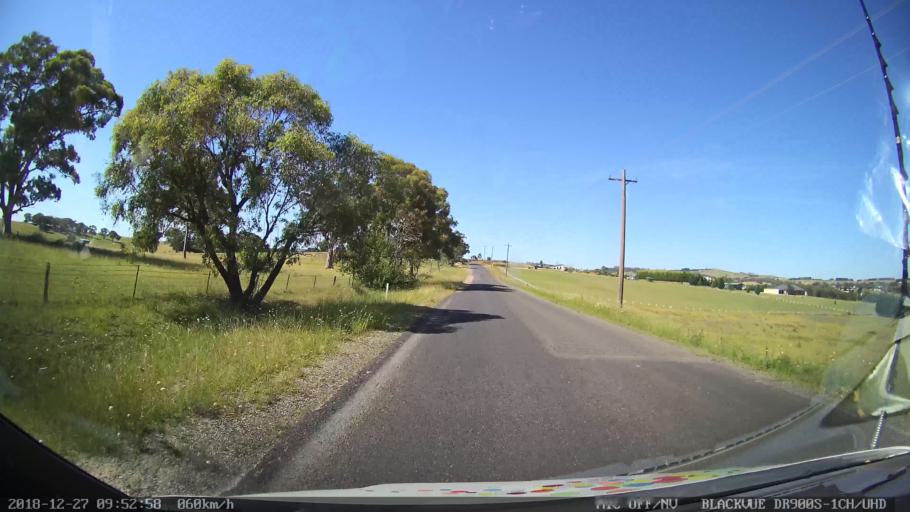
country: AU
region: New South Wales
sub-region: Lithgow
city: Portland
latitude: -33.3770
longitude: 149.9888
